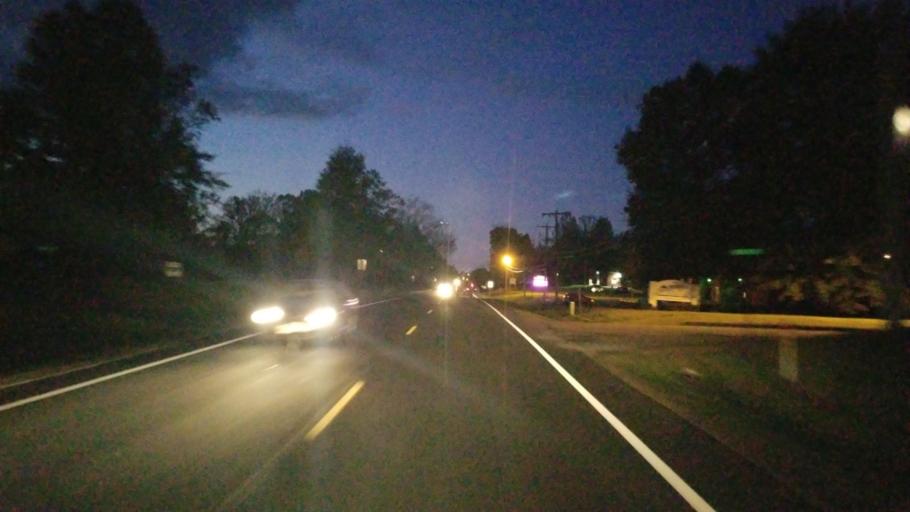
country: US
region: Ohio
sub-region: Vinton County
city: McArthur
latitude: 39.2622
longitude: -82.4766
